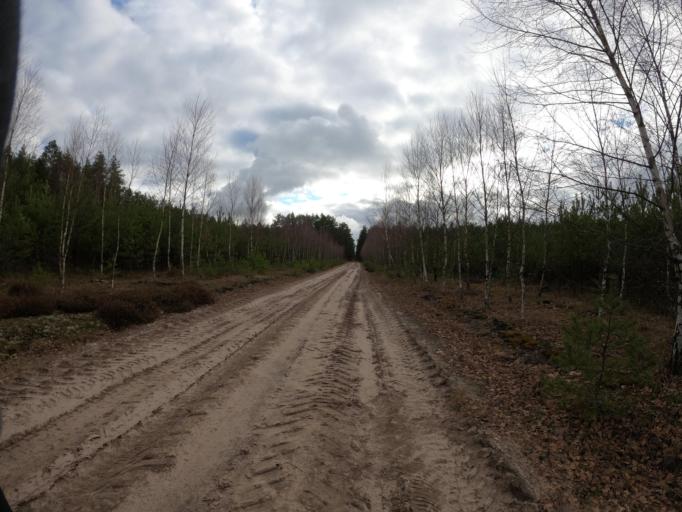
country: PL
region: Greater Poland Voivodeship
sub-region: Powiat zlotowski
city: Sypniewo
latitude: 53.4479
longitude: 16.5328
